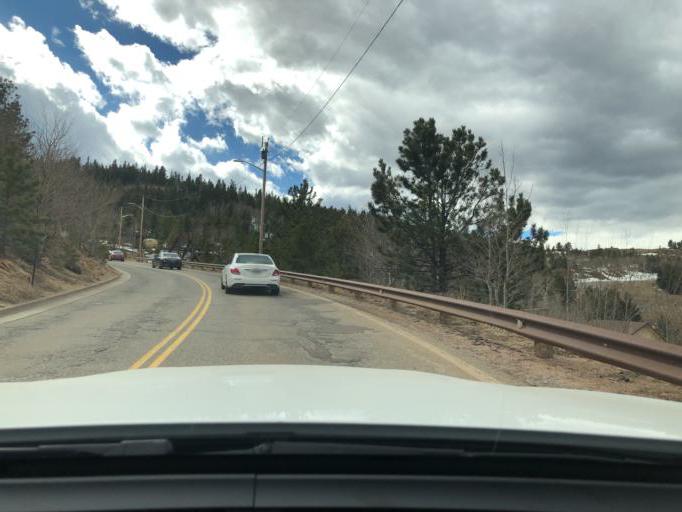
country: US
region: Colorado
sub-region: Gilpin County
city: Central City
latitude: 39.7954
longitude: -105.5123
